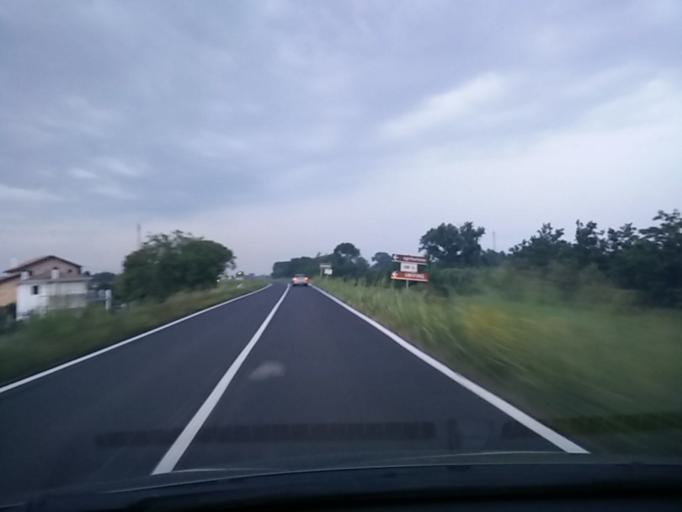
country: IT
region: Veneto
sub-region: Provincia di Venezia
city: Passarella
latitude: 45.5892
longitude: 12.6358
